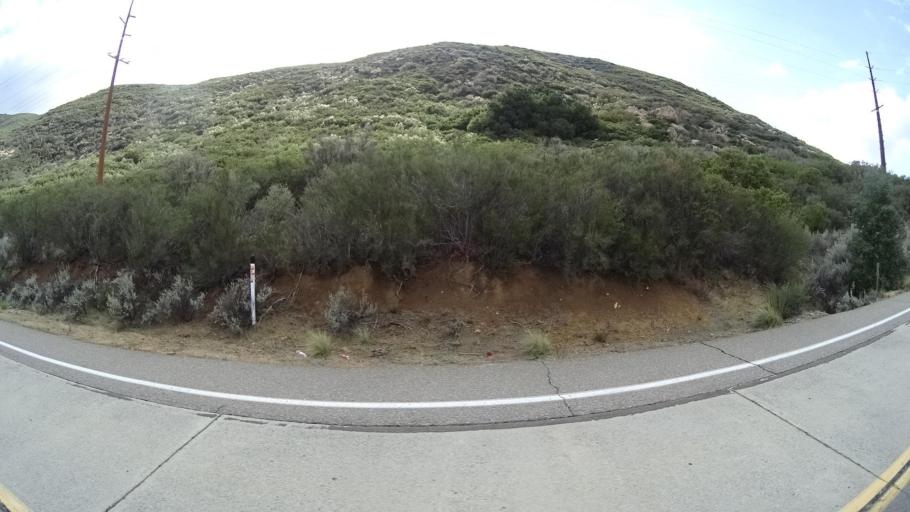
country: US
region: California
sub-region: San Diego County
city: Pine Valley
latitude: 32.8064
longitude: -116.5082
